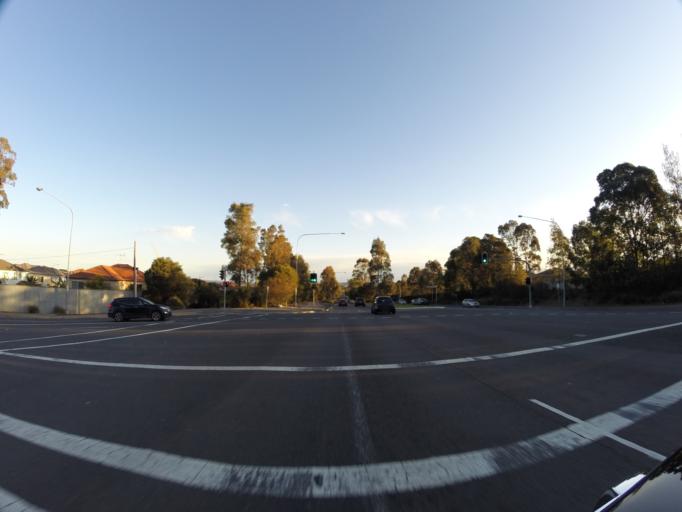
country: AU
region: New South Wales
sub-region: Fairfield
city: Cecil Park
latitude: -33.8892
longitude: 150.8609
